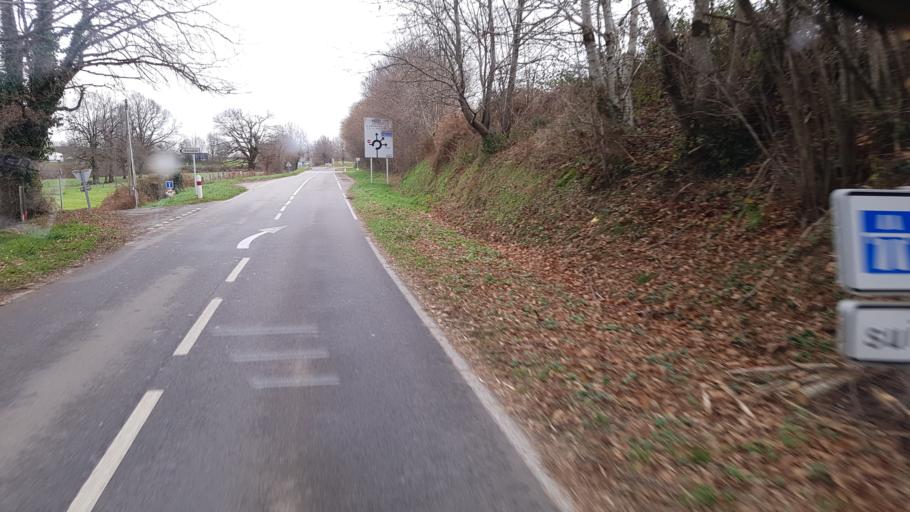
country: FR
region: Limousin
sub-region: Departement de la Correze
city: Donzenac
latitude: 45.2469
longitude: 1.5366
